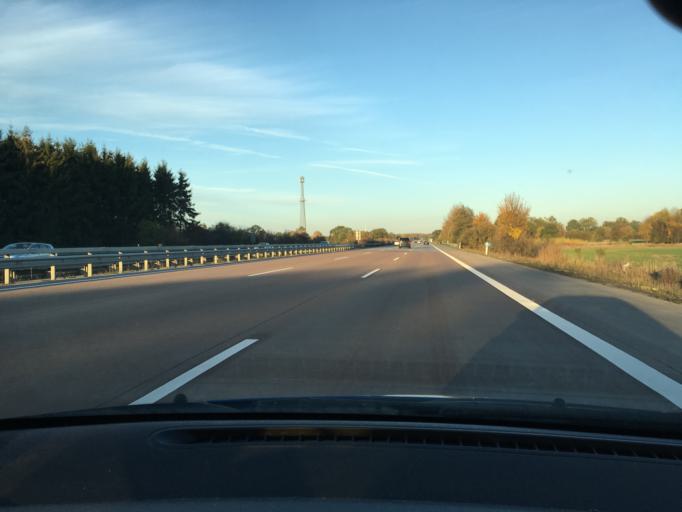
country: DE
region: Schleswig-Holstein
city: Braak
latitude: 53.6229
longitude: 10.2395
